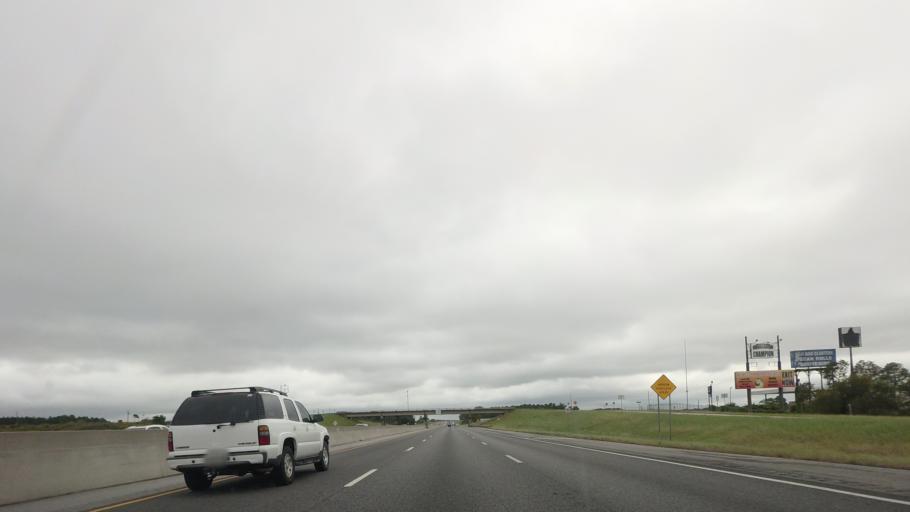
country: US
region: Georgia
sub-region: Turner County
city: Ashburn
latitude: 31.6281
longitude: -83.5776
